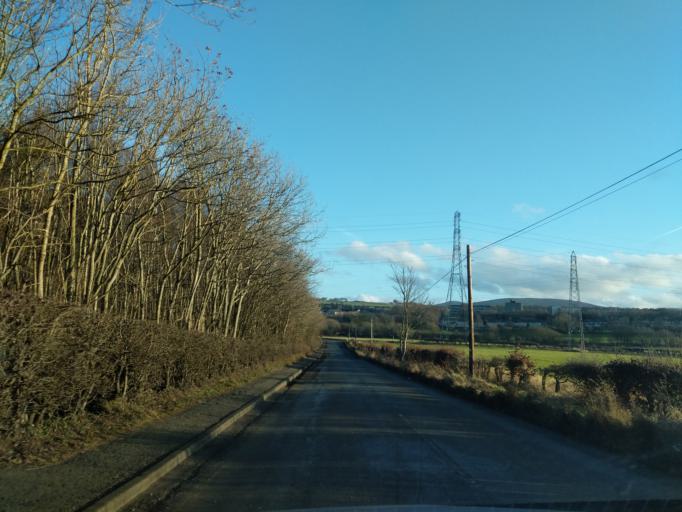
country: GB
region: Scotland
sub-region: Edinburgh
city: Currie
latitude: 55.9028
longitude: -3.3233
